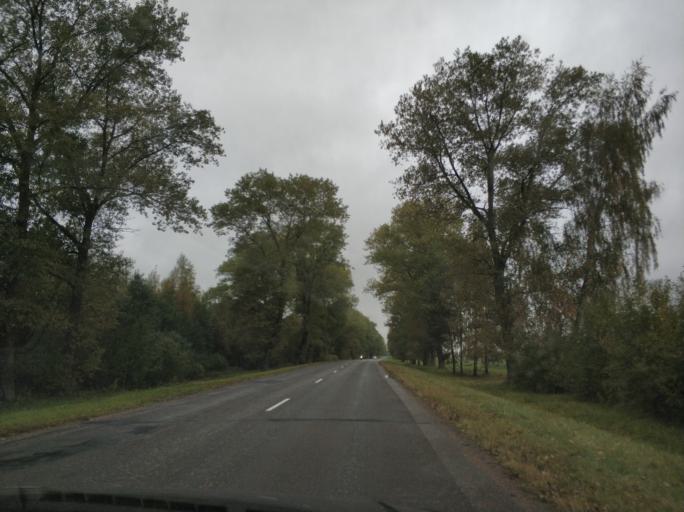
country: BY
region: Vitebsk
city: Polatsk
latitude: 55.4331
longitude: 28.9856
